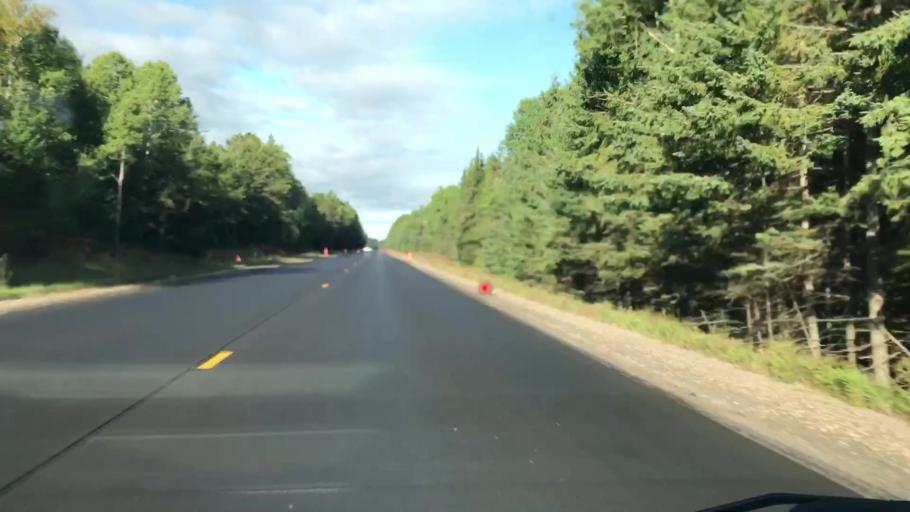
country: US
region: Michigan
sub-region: Mackinac County
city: Saint Ignace
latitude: 46.3459
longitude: -84.9311
